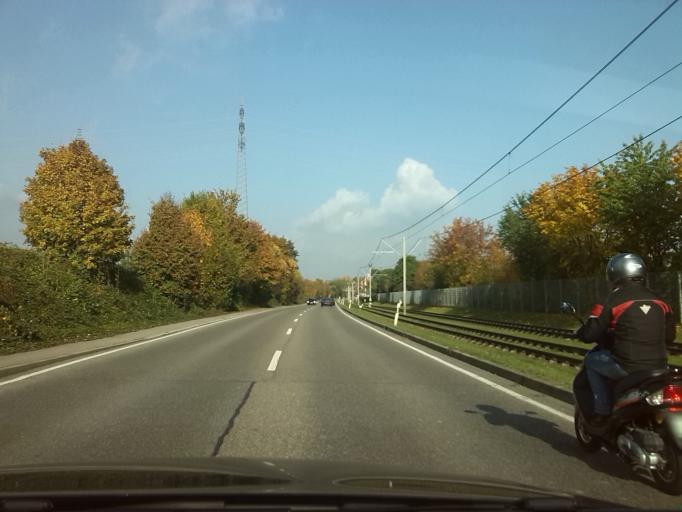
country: DE
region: Baden-Wuerttemberg
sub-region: Regierungsbezirk Stuttgart
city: Stuttgart Muehlhausen
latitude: 48.8519
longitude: 9.2448
